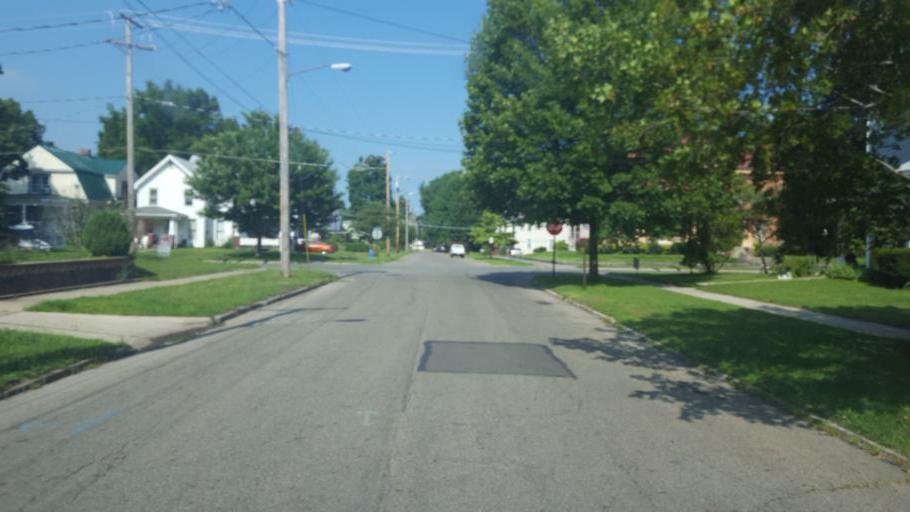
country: US
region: Ohio
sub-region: Crawford County
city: Galion
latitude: 40.7311
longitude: -82.7925
